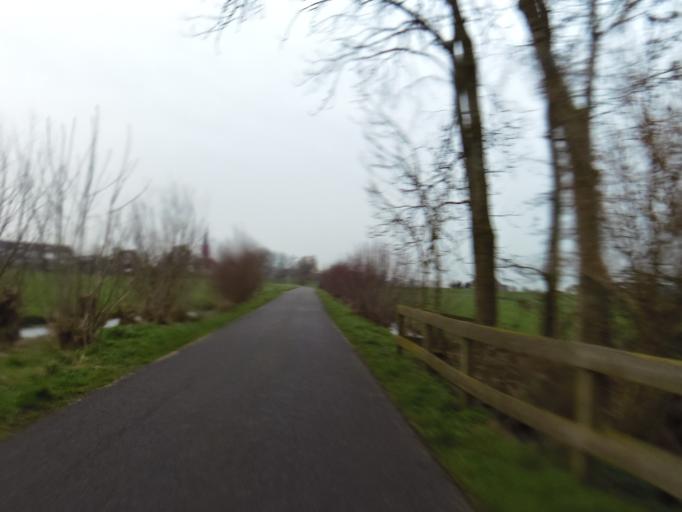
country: NL
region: South Holland
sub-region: Gemeente Leiderdorp
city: Leiderdorp
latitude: 52.1885
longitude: 4.5671
